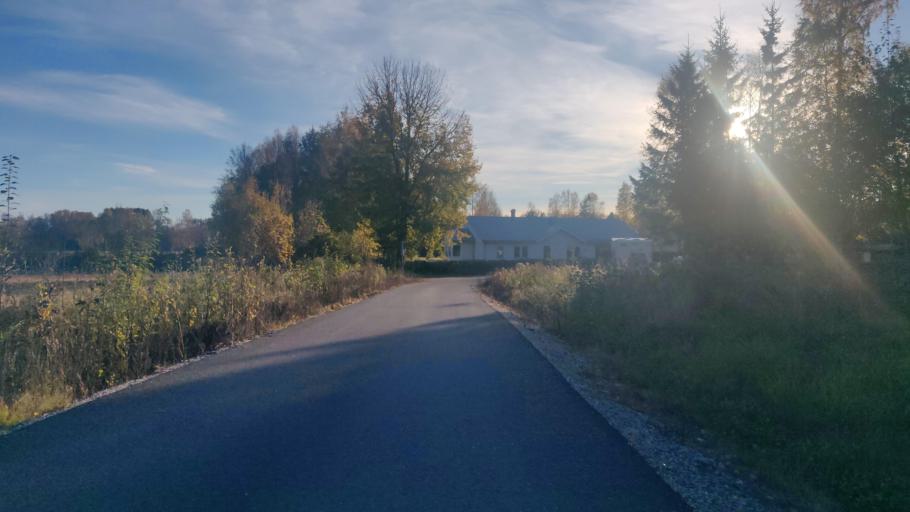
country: SE
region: Vaesternorrland
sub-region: Sundsvalls Kommun
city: Skottsund
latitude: 62.2901
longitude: 17.3947
